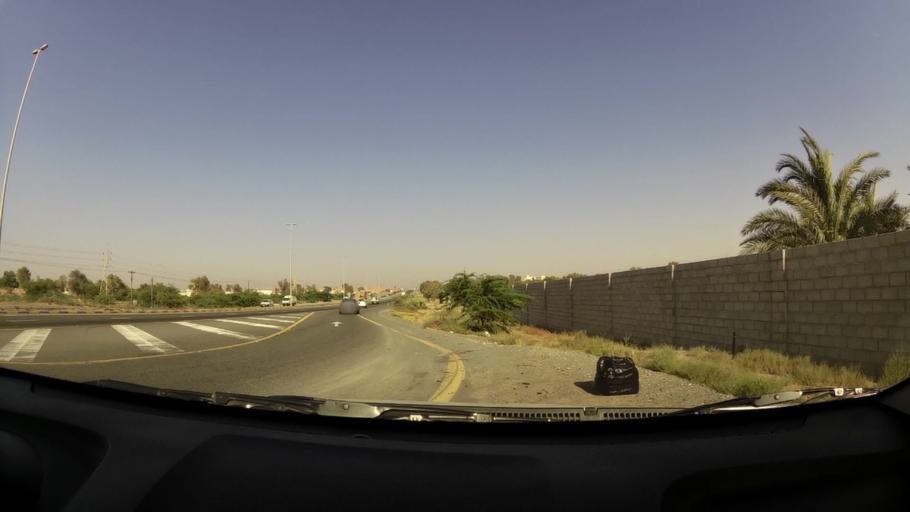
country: AE
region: Umm al Qaywayn
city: Umm al Qaywayn
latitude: 25.4439
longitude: 55.6289
